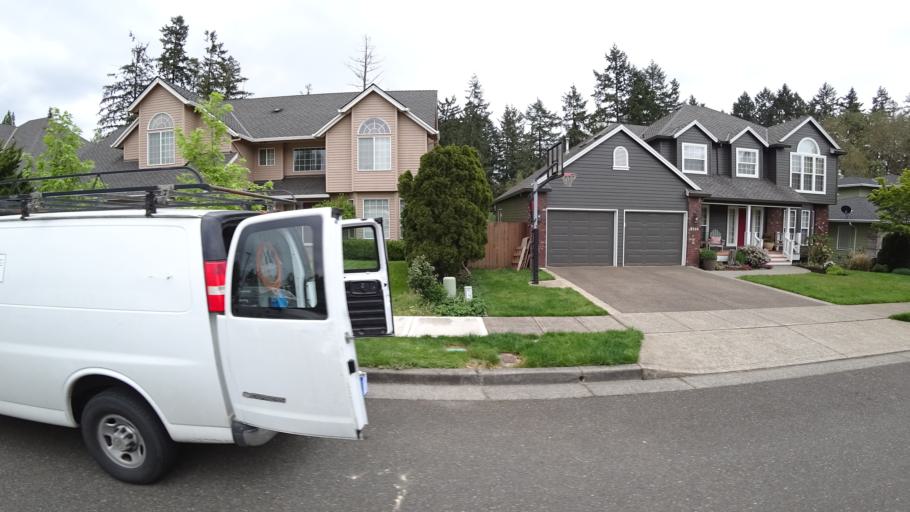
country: US
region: Oregon
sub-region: Washington County
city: Beaverton
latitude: 45.4614
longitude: -122.8347
